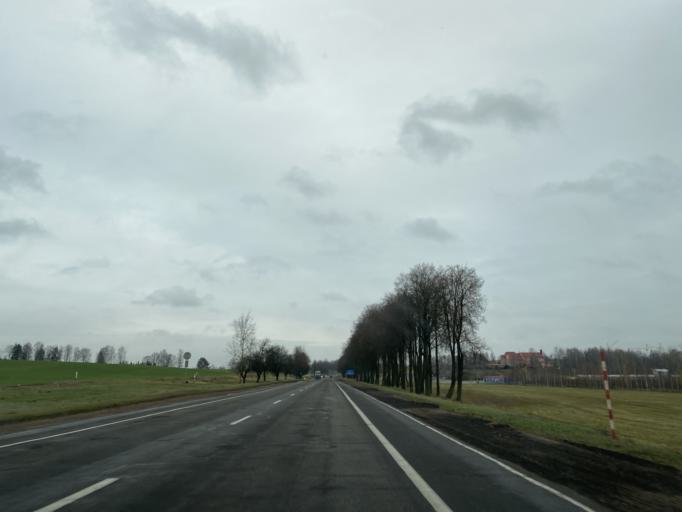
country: BY
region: Minsk
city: Horad Smalyavichy
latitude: 54.0442
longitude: 28.0604
